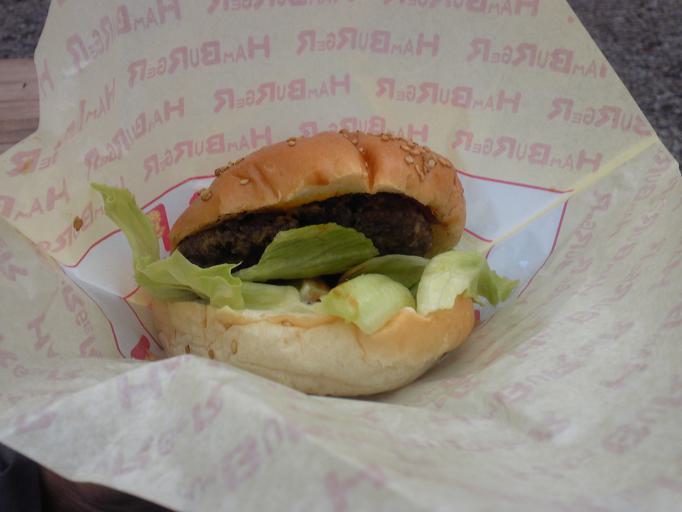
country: JP
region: Hokkaido
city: Shibetsu
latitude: 44.1222
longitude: 145.0801
